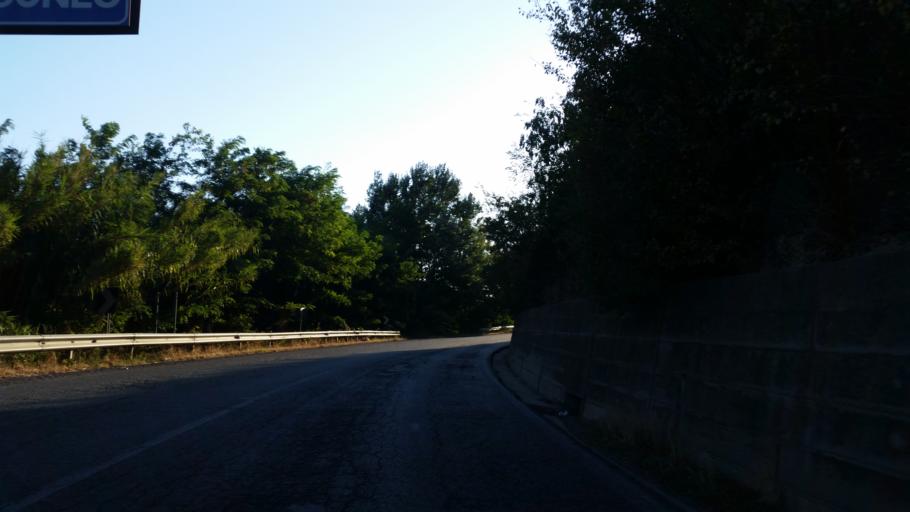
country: IT
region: Piedmont
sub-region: Provincia di Asti
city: Canelli
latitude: 44.7125
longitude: 8.2654
